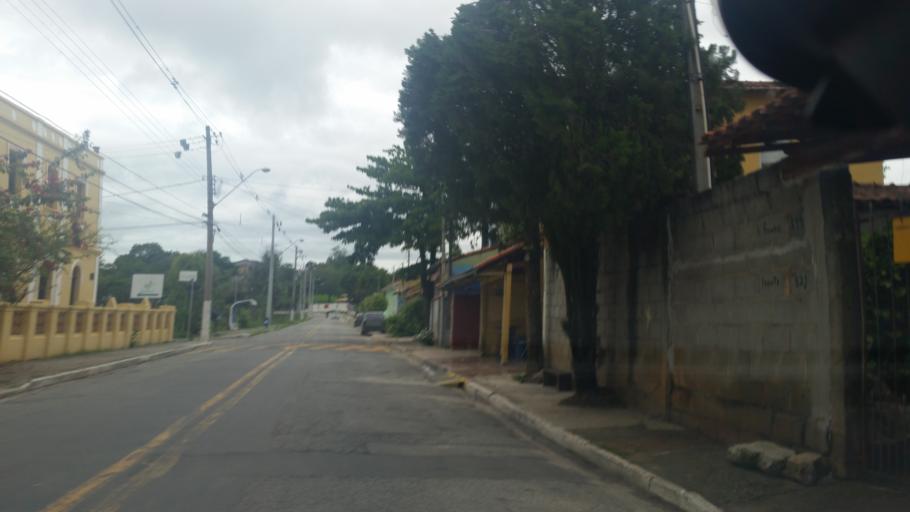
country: BR
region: Sao Paulo
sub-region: Taubate
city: Taubate
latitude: -23.0237
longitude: -45.6339
